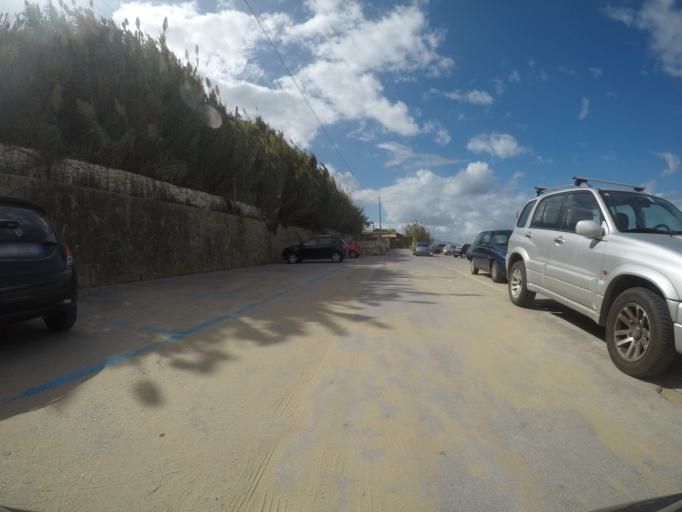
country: IT
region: Sicily
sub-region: Palermo
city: Trappeto
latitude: 38.0630
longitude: 13.0299
